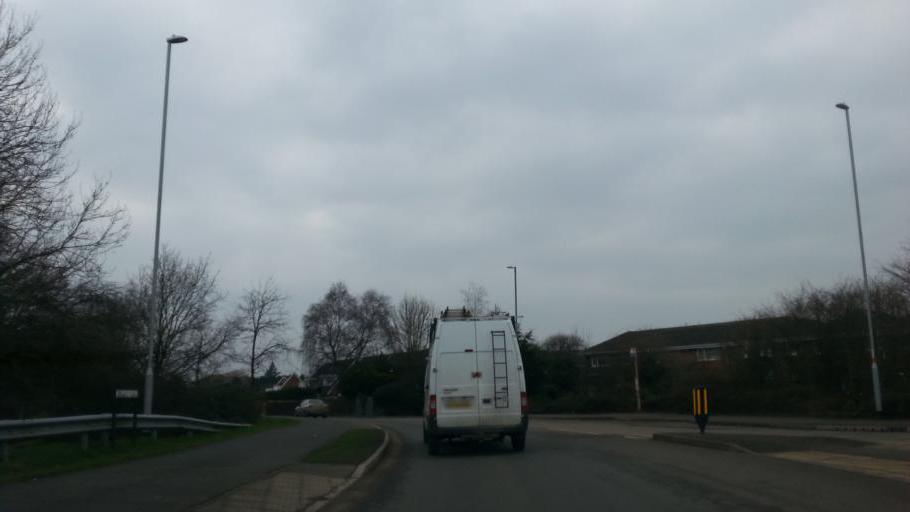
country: GB
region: England
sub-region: Northamptonshire
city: Corby
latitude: 52.4801
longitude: -0.7041
